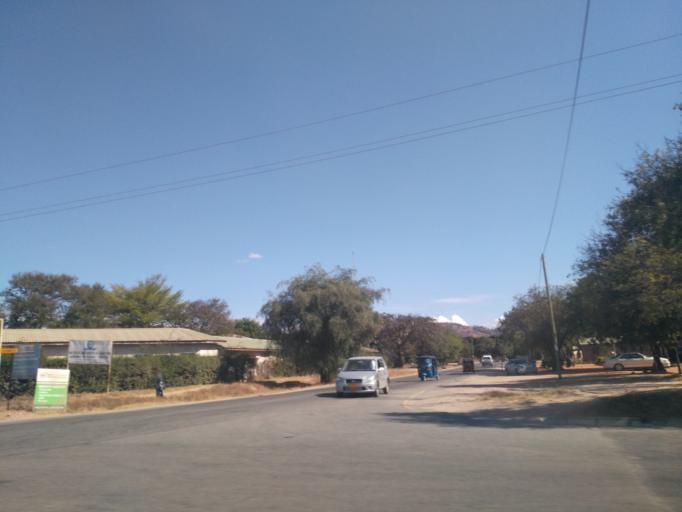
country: TZ
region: Dodoma
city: Dodoma
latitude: -6.1838
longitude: 35.7462
